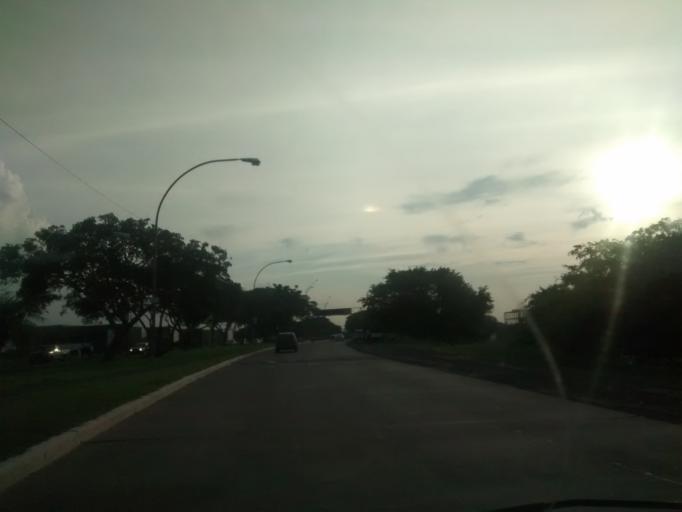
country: AR
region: Chaco
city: Resistencia
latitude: -27.4281
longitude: -58.9610
